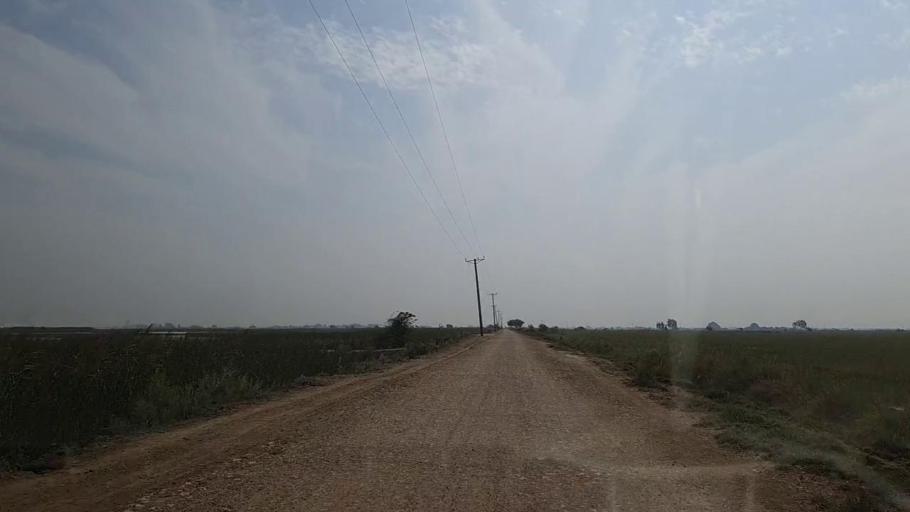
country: PK
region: Sindh
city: Mirpur Batoro
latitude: 24.6052
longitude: 68.2113
